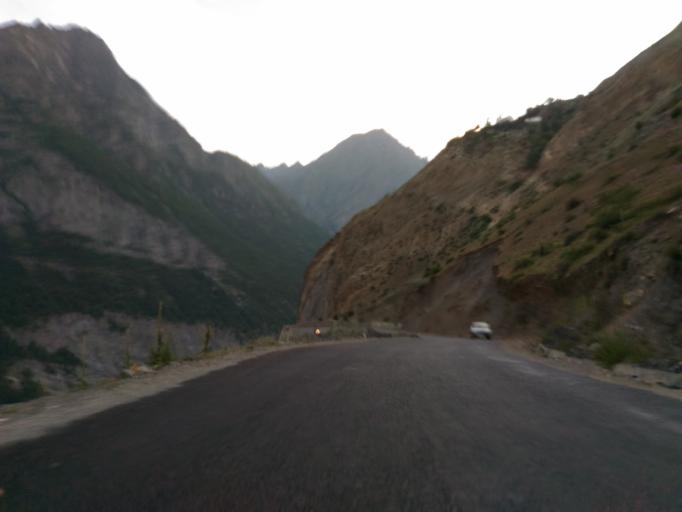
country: IN
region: Himachal Pradesh
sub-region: Lahul and Spiti
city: Kyelang
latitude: 32.5116
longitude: 77.0064
